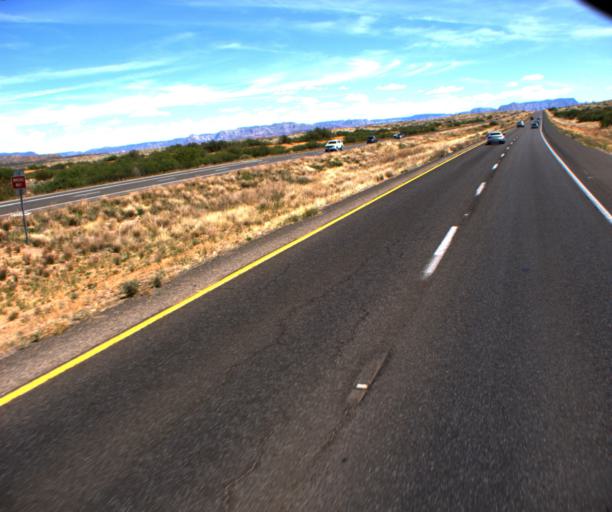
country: US
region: Arizona
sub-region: Yavapai County
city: Cottonwood
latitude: 34.7451
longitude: -111.9672
